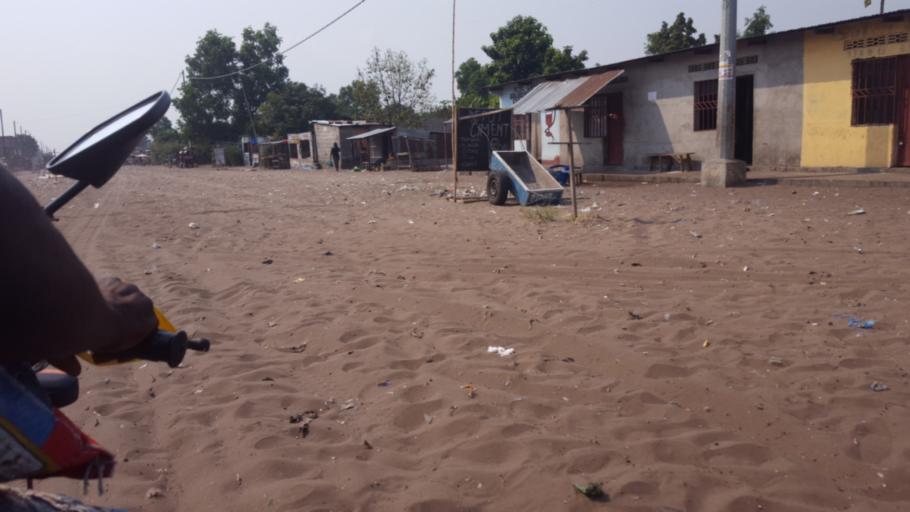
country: CD
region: Kinshasa
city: Masina
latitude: -4.3650
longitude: 15.5117
